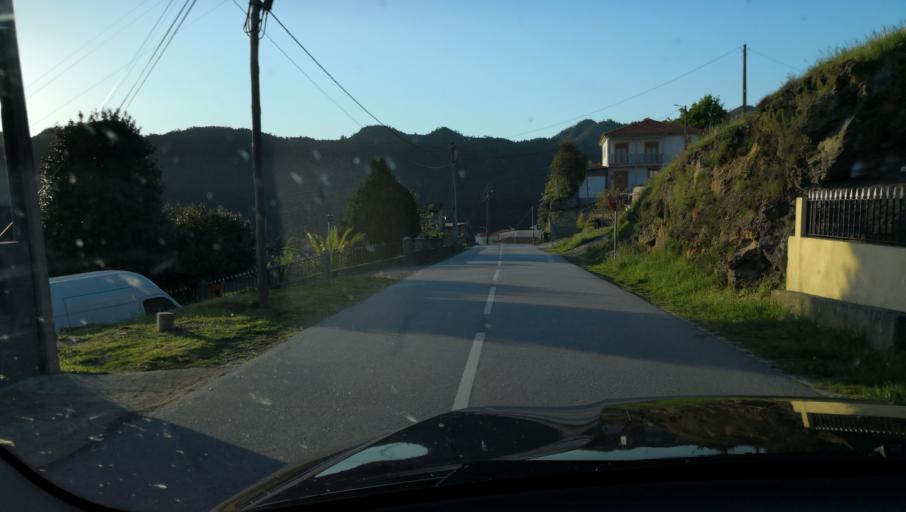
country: PT
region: Vila Real
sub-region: Mondim de Basto
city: Mondim de Basto
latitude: 41.4123
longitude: -7.8782
